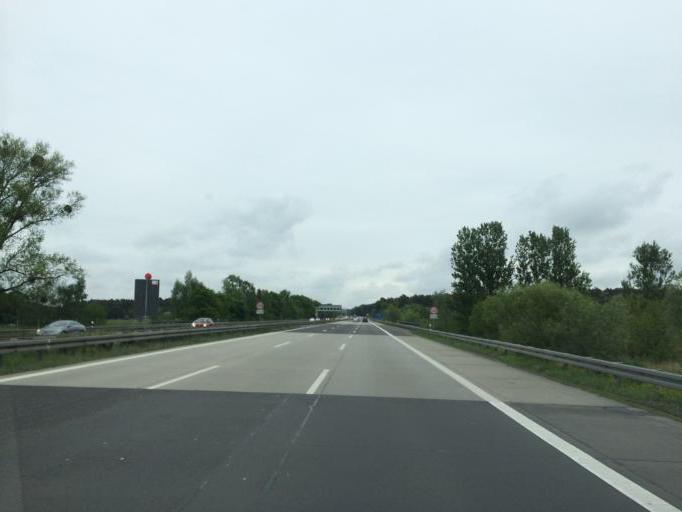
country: DE
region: Brandenburg
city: Potsdam
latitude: 52.3329
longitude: 13.1212
